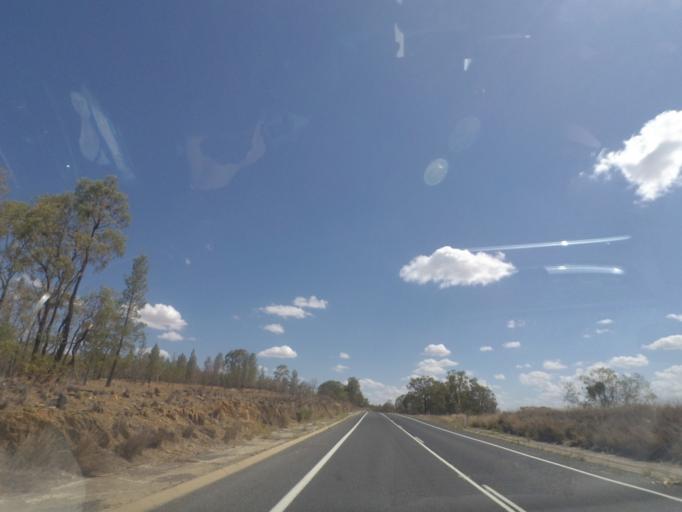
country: AU
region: Queensland
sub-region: Southern Downs
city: Warwick
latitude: -28.2246
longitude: 151.5527
